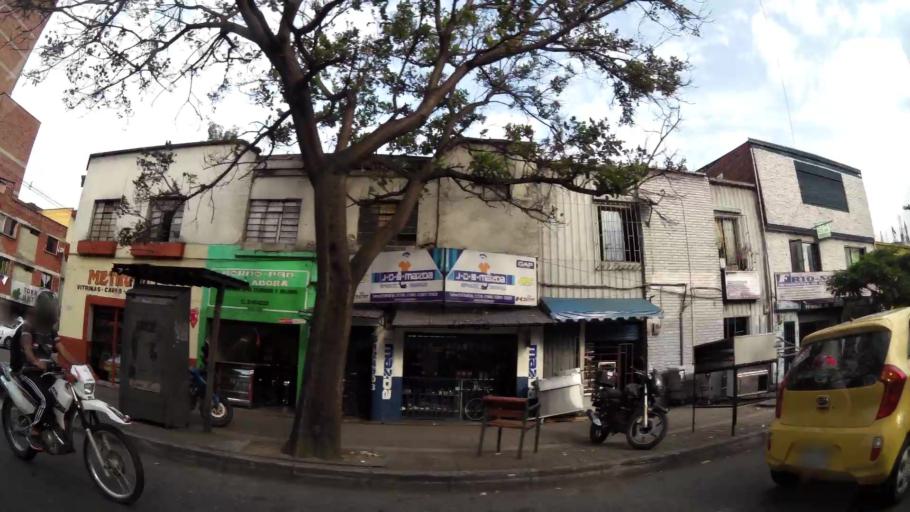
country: CO
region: Antioquia
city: Medellin
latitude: 6.2587
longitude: -75.5674
